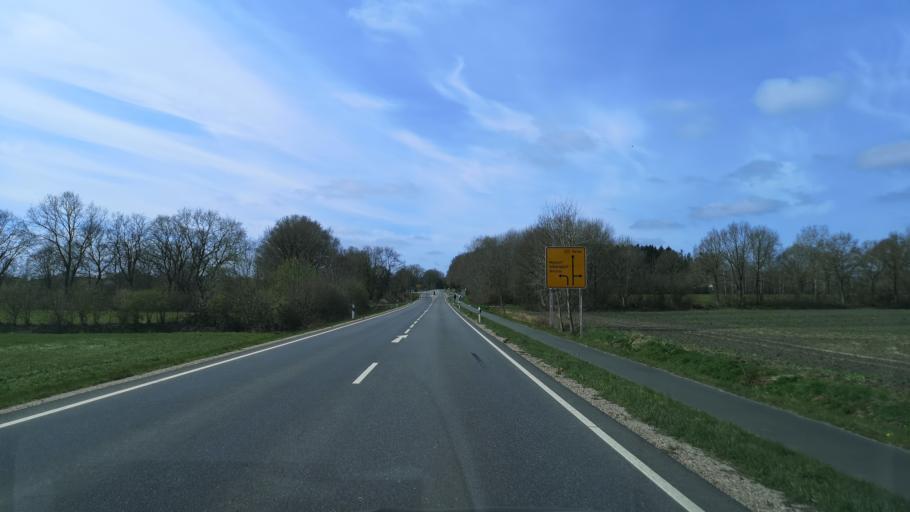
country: DE
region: Schleswig-Holstein
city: Wrohm
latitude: 54.2170
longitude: 9.3867
